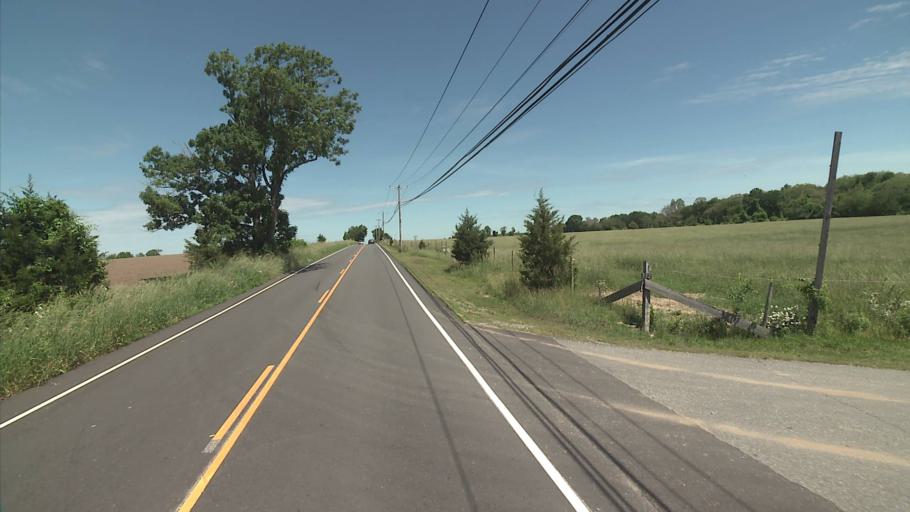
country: US
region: Connecticut
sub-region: Windham County
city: Moosup
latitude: 41.6673
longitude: -71.8475
